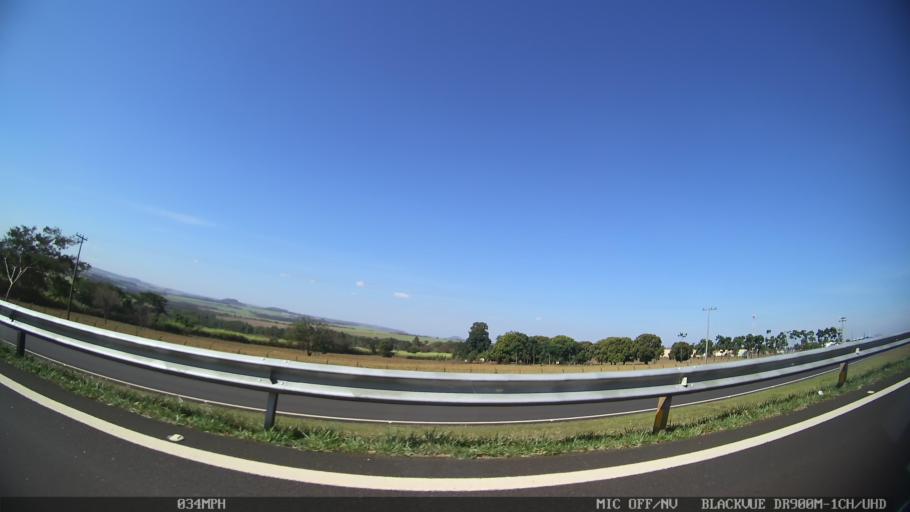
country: BR
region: Sao Paulo
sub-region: Jardinopolis
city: Jardinopolis
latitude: -21.0930
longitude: -47.7929
